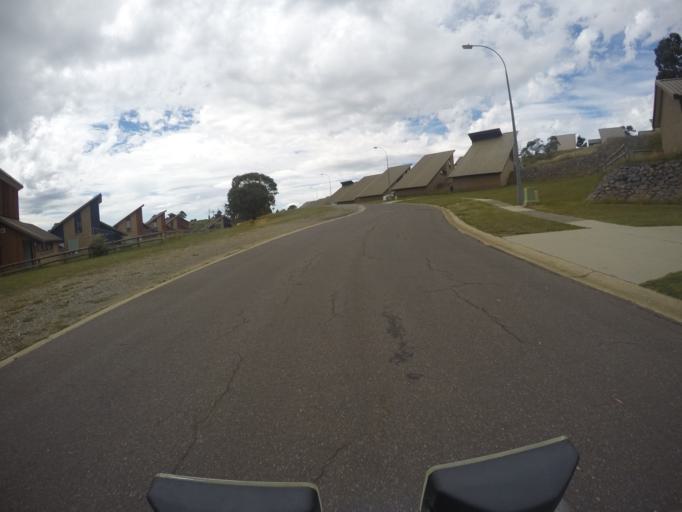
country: AU
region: New South Wales
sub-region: Snowy River
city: Jindabyne
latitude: -35.9341
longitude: 148.3807
